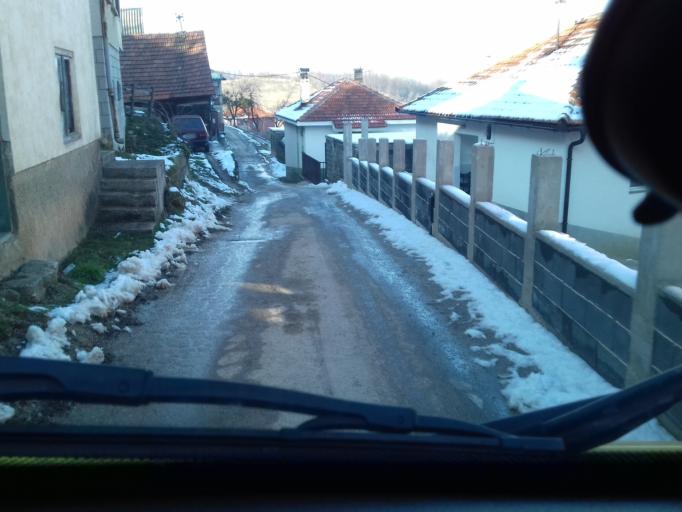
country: BA
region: Federation of Bosnia and Herzegovina
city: Zenica
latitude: 44.1775
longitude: 17.8806
